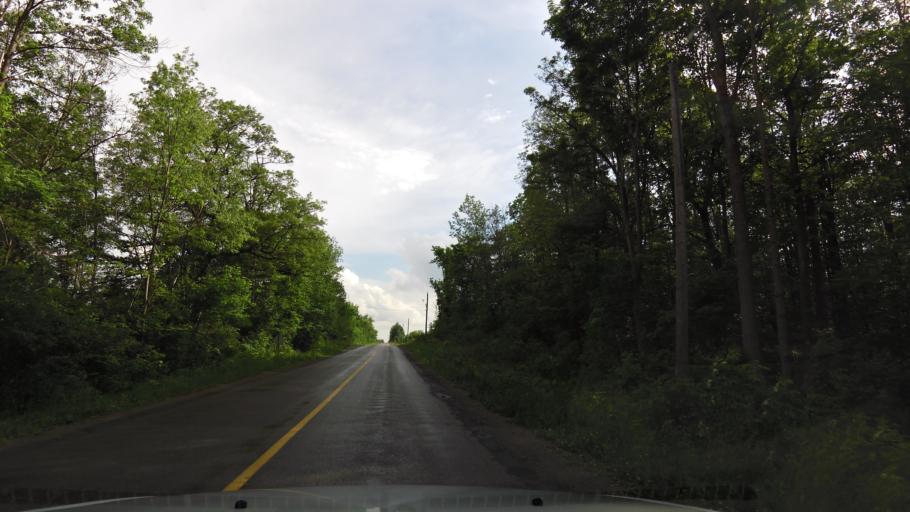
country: CA
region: Ontario
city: Ancaster
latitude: 43.0094
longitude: -80.0563
